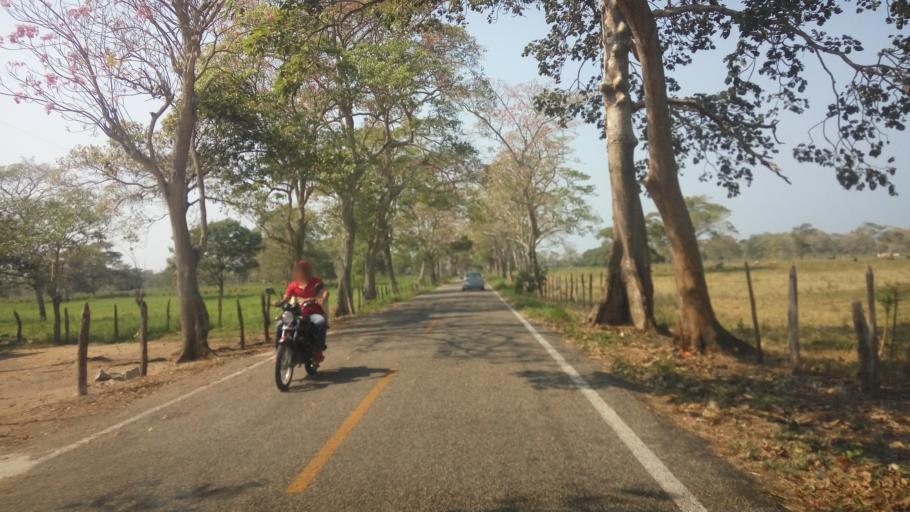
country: MX
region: Tabasco
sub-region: Centla
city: Alvaro Obregon 2da. Seccion (El Lechugal)
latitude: 18.4741
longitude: -92.7674
